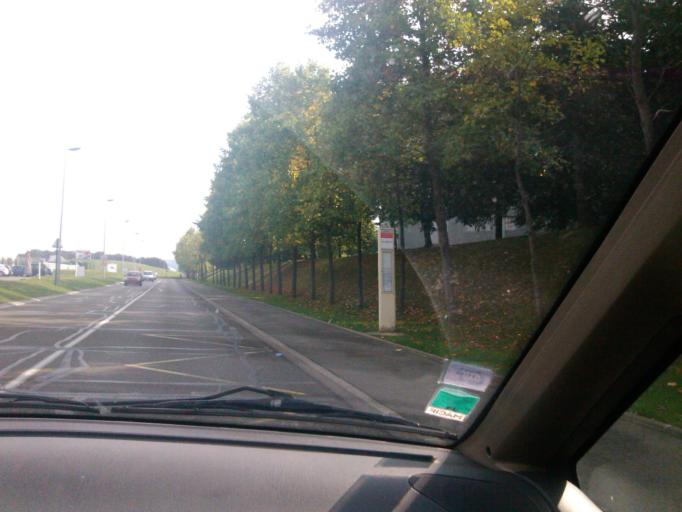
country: FR
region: Ile-de-France
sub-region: Departement des Yvelines
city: Plaisir
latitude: 48.8294
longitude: 1.9513
